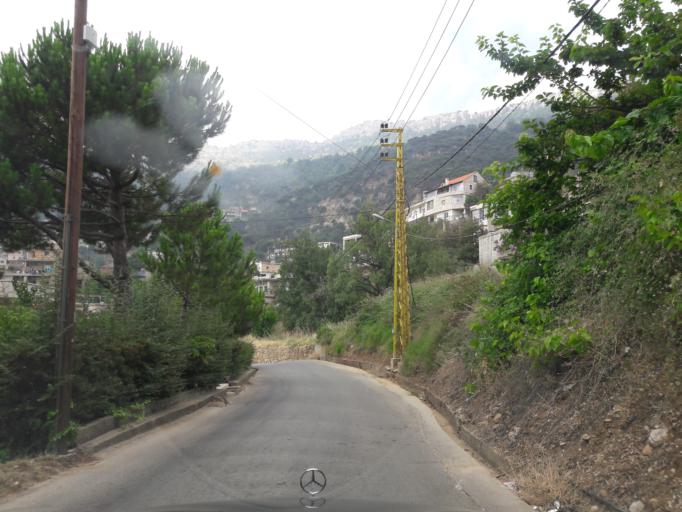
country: LB
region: Beqaa
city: Zahle
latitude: 33.9434
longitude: 35.7997
